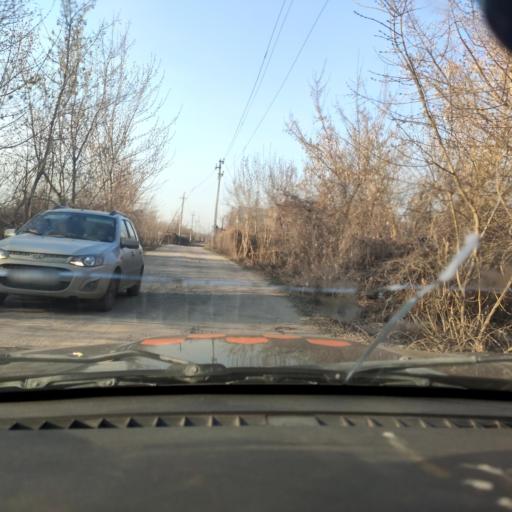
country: RU
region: Samara
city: Tol'yatti
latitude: 53.5847
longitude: 49.2742
